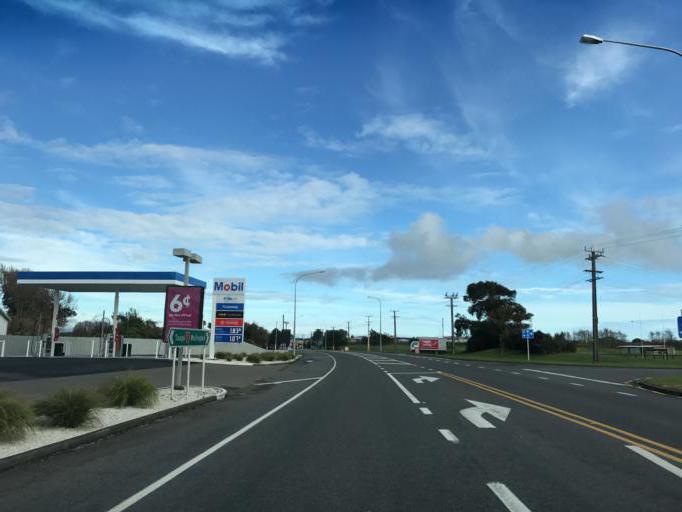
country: NZ
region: Manawatu-Wanganui
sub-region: Horowhenua District
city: Foxton
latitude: -40.4645
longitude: 175.2894
